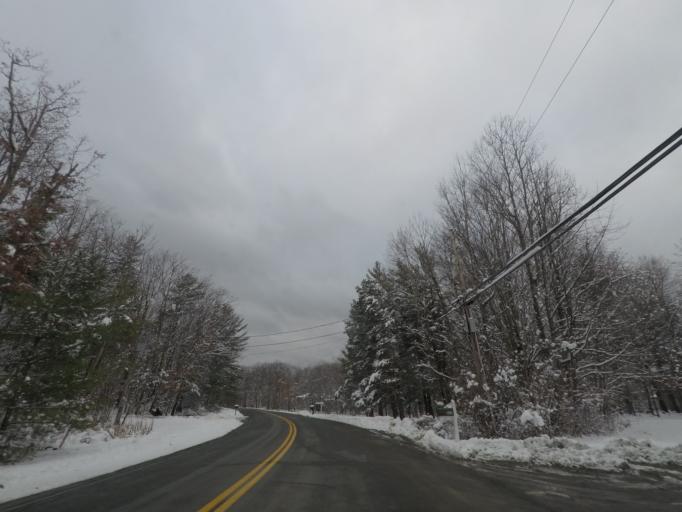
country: US
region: New York
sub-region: Rensselaer County
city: Averill Park
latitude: 42.6680
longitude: -73.5218
